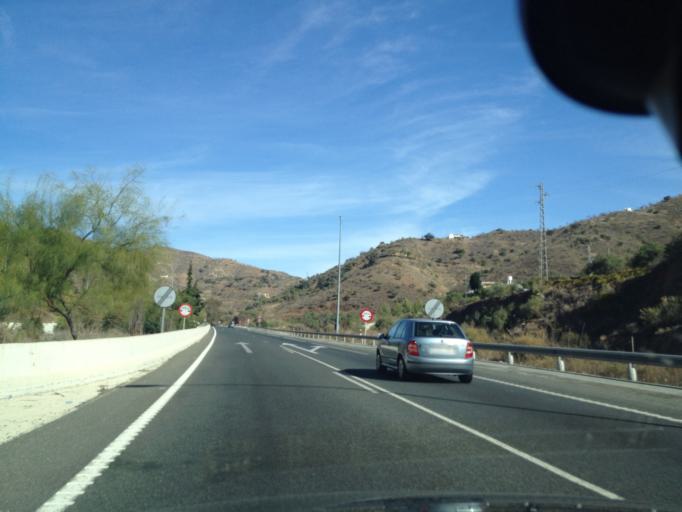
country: ES
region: Andalusia
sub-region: Provincia de Malaga
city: Casabermeja
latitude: 36.8637
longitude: -4.4361
